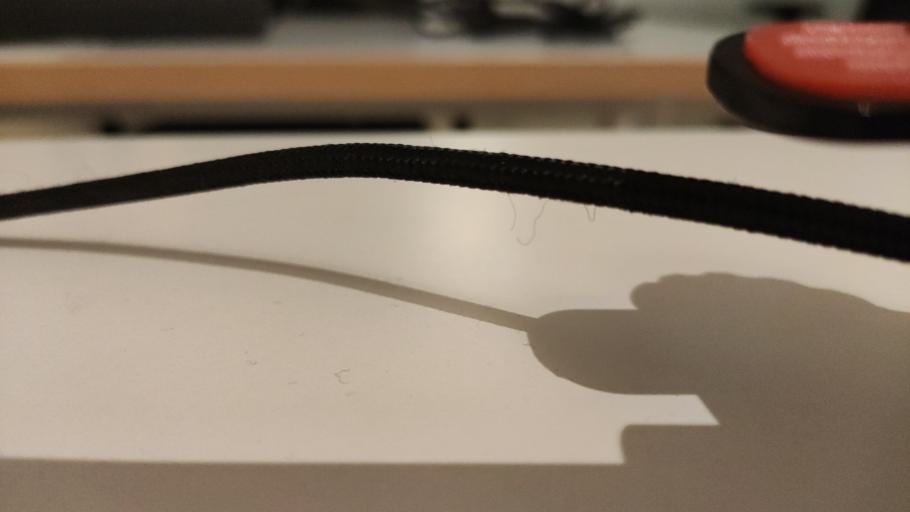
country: RU
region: Moskovskaya
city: Kurovskoye
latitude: 55.5840
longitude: 38.8908
